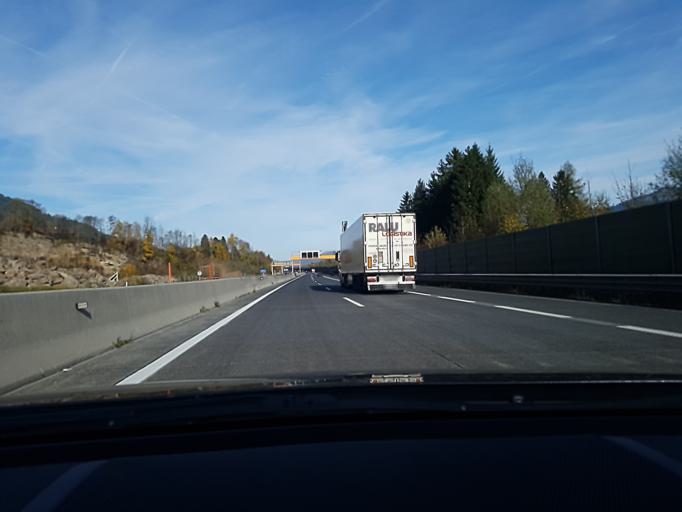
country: AT
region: Salzburg
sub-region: Politischer Bezirk Hallein
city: Golling an der Salzach
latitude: 47.5943
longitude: 13.1520
